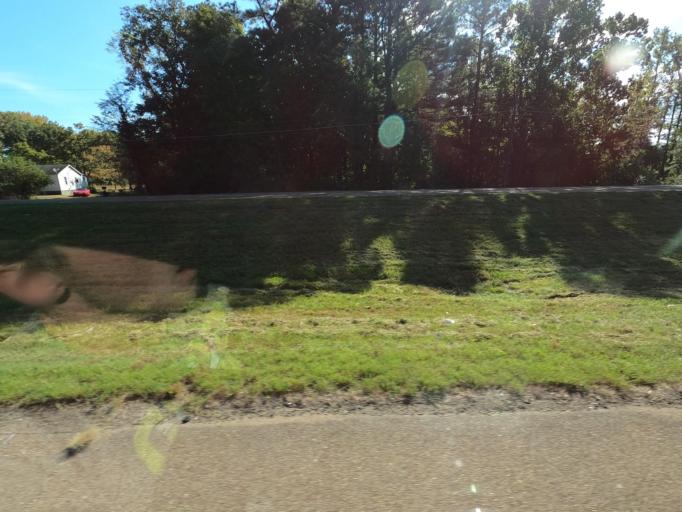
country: US
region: Tennessee
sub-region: Shelby County
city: Millington
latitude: 35.3911
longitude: -89.8553
